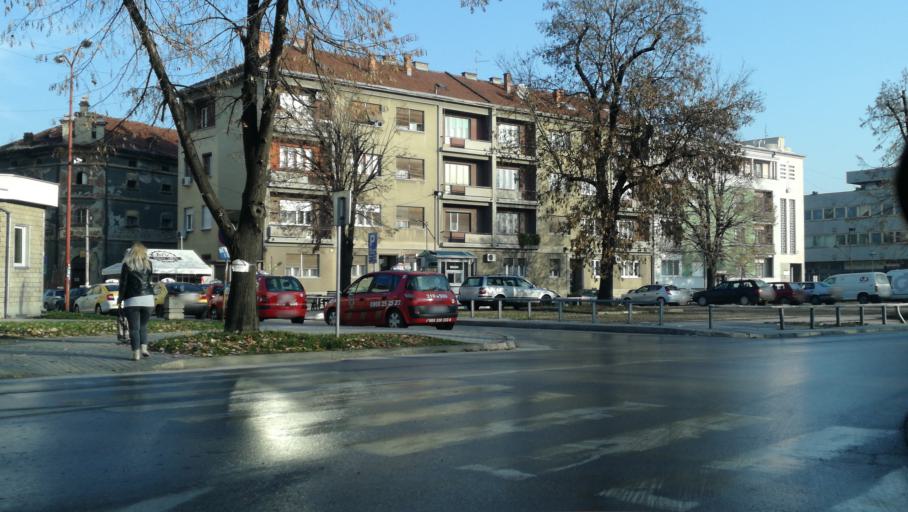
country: RS
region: Central Serbia
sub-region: Moravicki Okrug
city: Cacak
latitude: 43.8902
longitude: 20.3526
